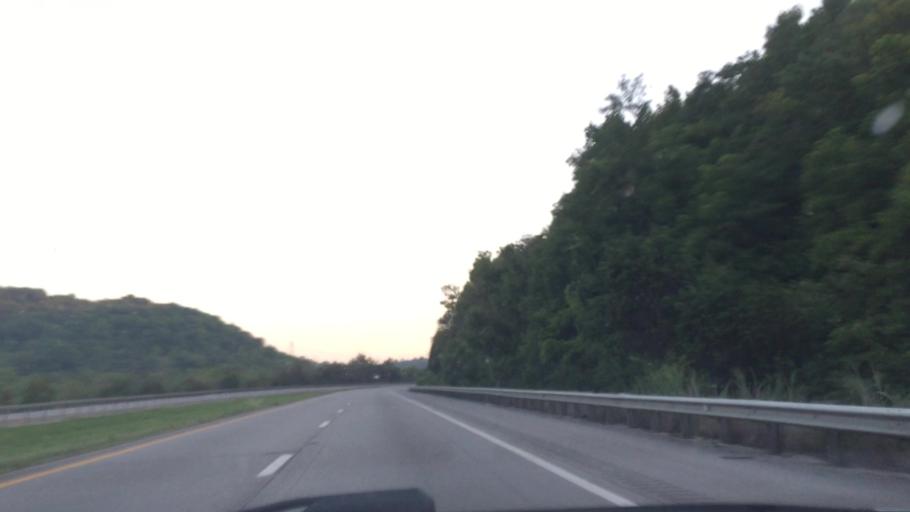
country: US
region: Kentucky
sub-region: Trimble County
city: Providence
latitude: 38.6082
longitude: -85.1688
